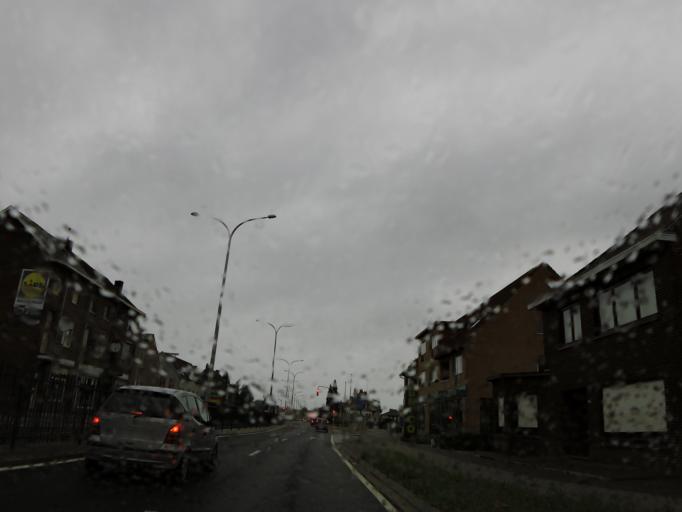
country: BE
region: Flanders
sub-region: Provincie Limburg
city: Maasmechelen
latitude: 50.9713
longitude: 5.6984
